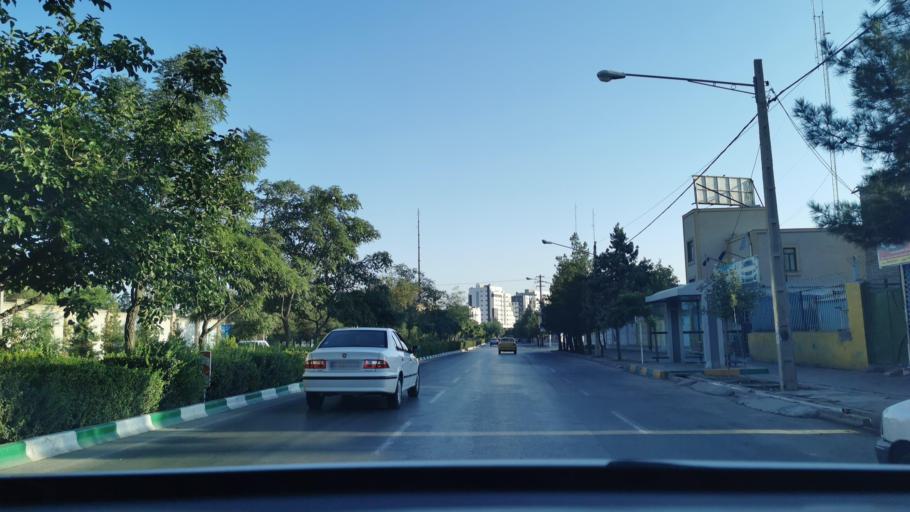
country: IR
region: Razavi Khorasan
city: Mashhad
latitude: 36.3558
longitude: 59.5129
